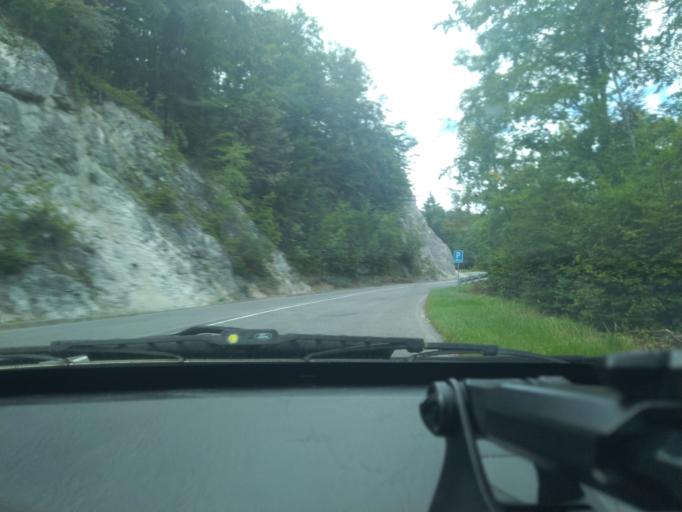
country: SK
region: Banskobystricky
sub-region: Okres Banska Bystrica
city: Banska Bystrica
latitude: 48.8247
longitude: 19.0225
